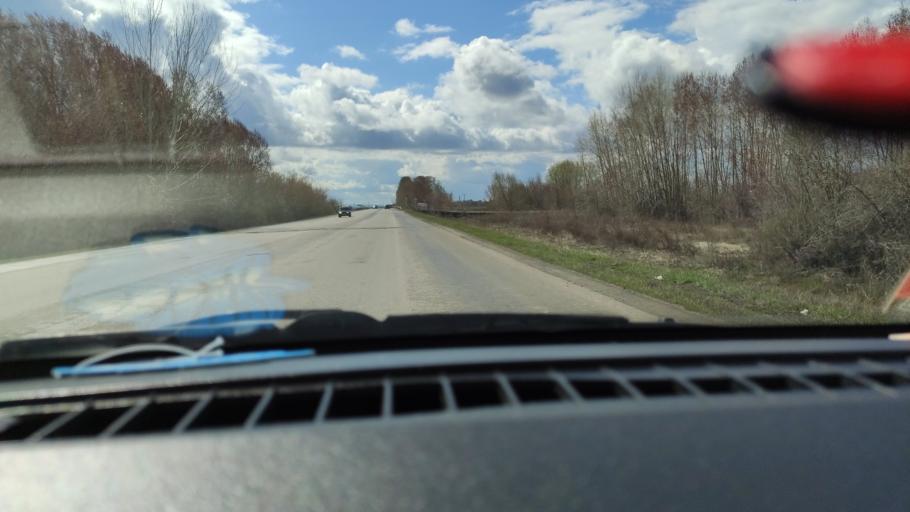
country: RU
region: Samara
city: Tol'yatti
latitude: 53.6926
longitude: 49.4187
